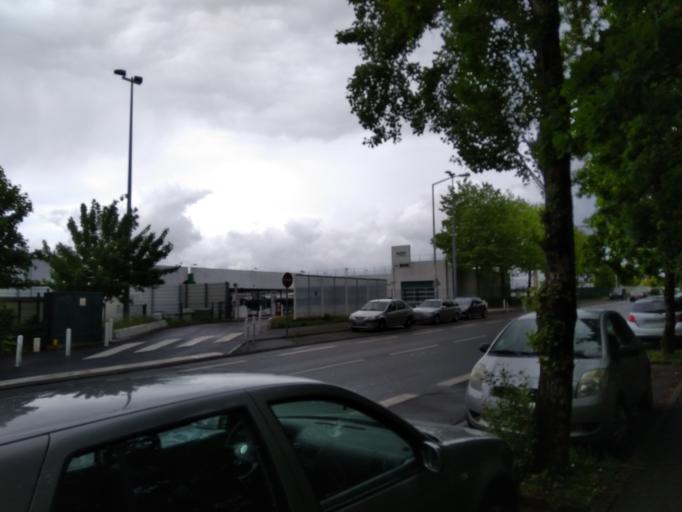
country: FR
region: Pays de la Loire
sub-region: Departement de la Loire-Atlantique
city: Orvault
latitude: 47.2464
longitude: -1.6164
